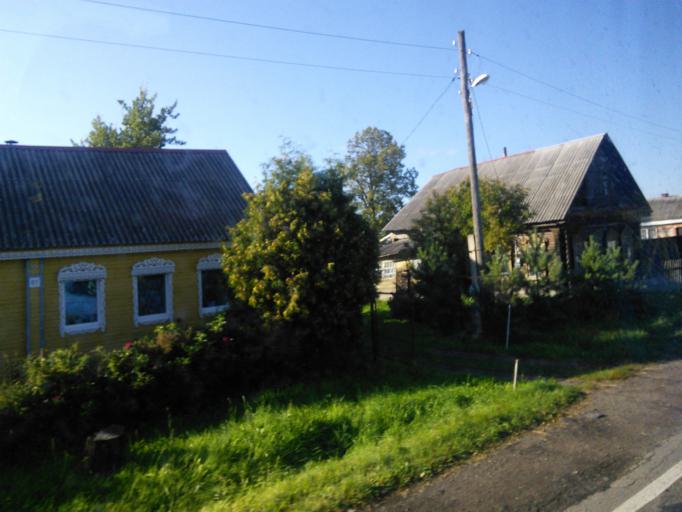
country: RU
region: Jaroslavl
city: Rybinsk
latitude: 58.2644
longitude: 38.8515
